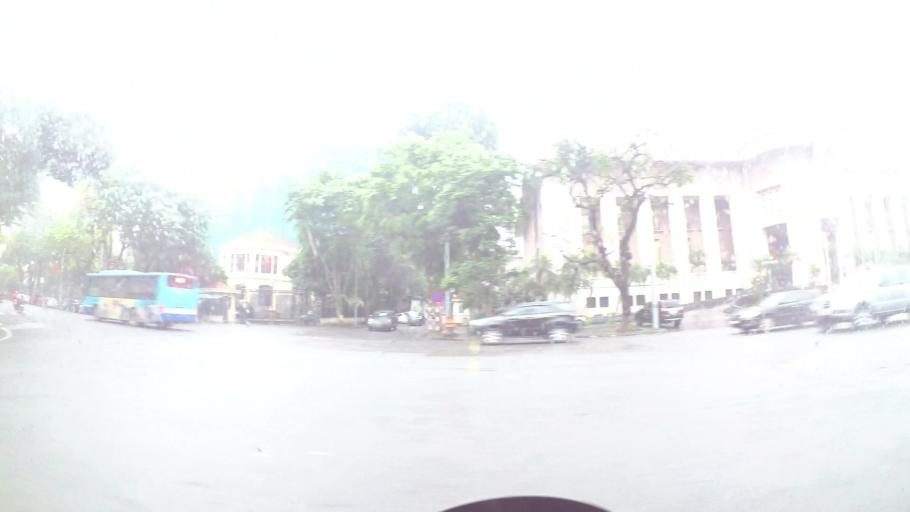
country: VN
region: Ha Noi
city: Hoan Kiem
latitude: 21.0276
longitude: 105.8560
